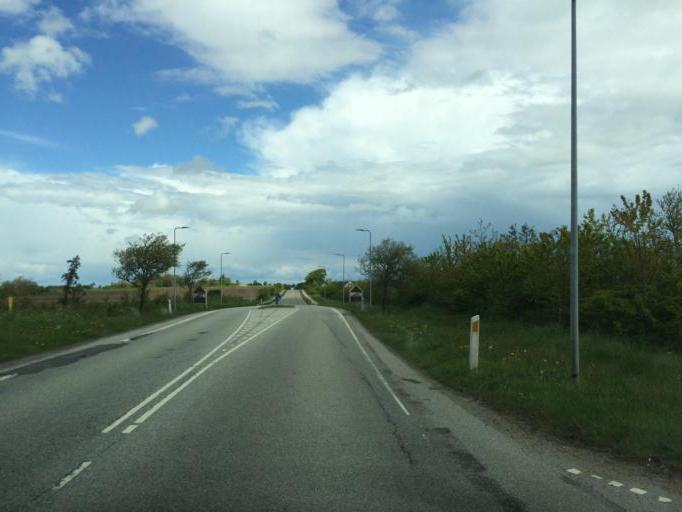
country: DK
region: North Denmark
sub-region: Vesthimmerland Kommune
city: Farso
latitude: 56.7287
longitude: 9.2926
